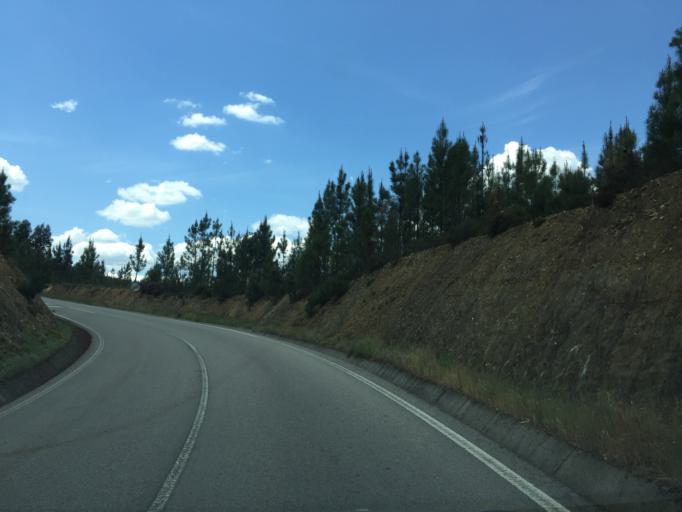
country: PT
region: Coimbra
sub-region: Pampilhosa da Serra
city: Pampilhosa da Serra
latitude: 40.0843
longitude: -7.7944
